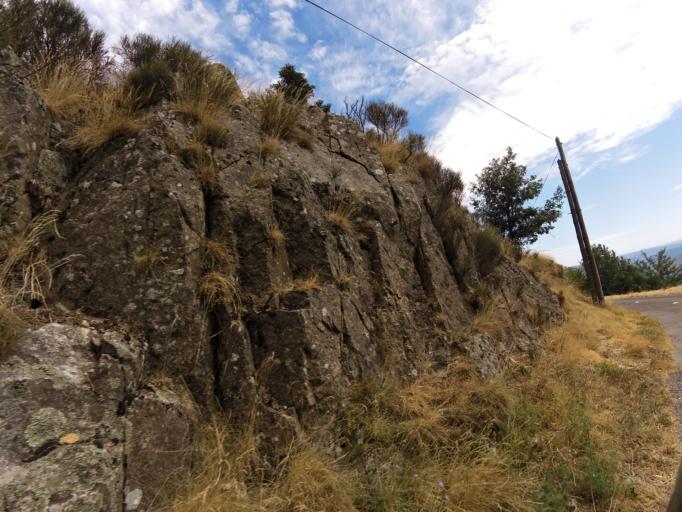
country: FR
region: Languedoc-Roussillon
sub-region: Departement du Gard
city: Le Vigan
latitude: 44.0362
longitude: 3.6090
